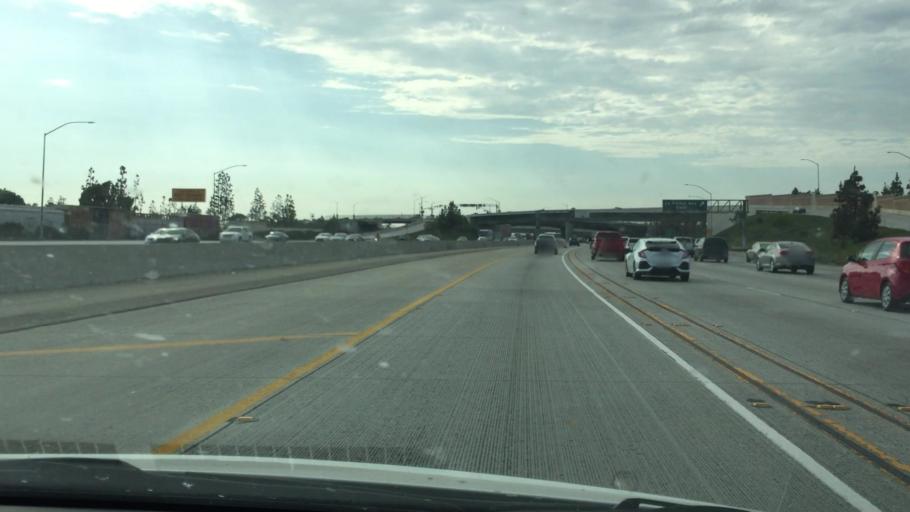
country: US
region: California
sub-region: Orange County
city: Fullerton
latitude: 33.8428
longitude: -117.9543
